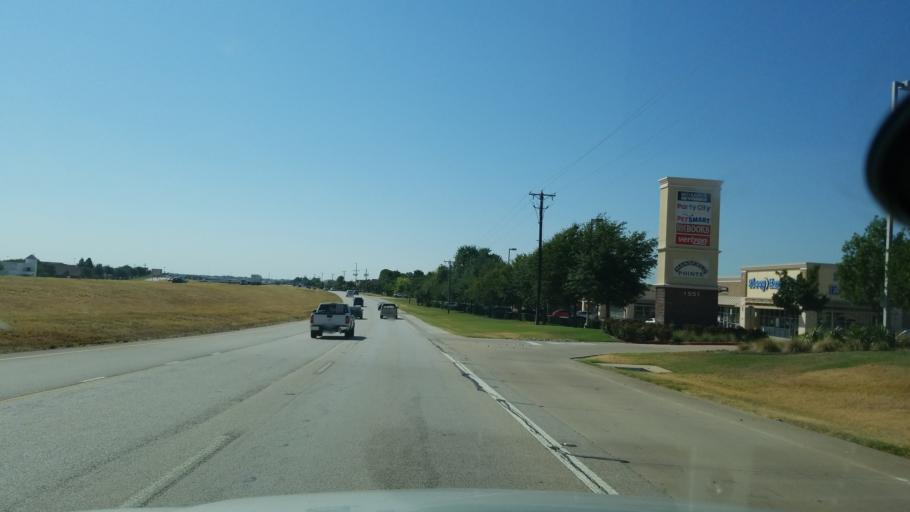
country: US
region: Texas
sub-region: Tarrant County
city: Mansfield
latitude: 32.5872
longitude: -97.1395
